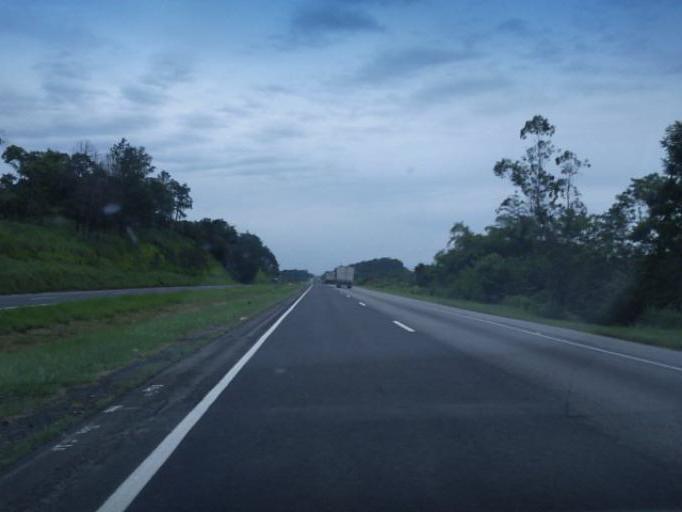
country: BR
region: Sao Paulo
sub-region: Registro
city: Registro
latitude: -24.4258
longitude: -47.7816
